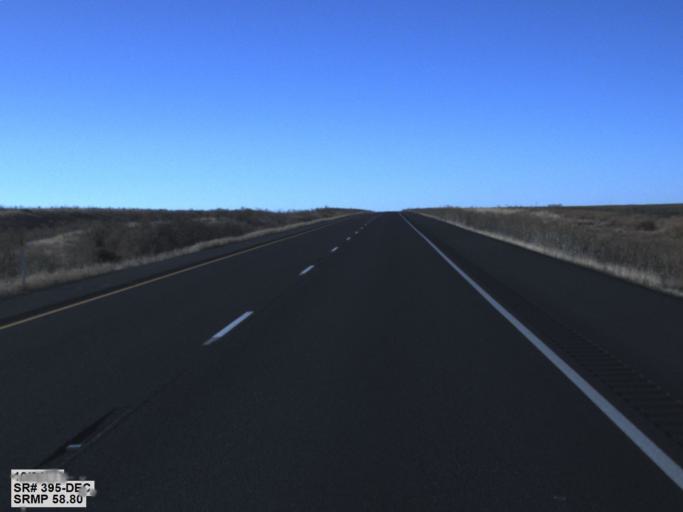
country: US
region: Washington
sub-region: Franklin County
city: Connell
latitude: 46.7037
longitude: -118.8365
